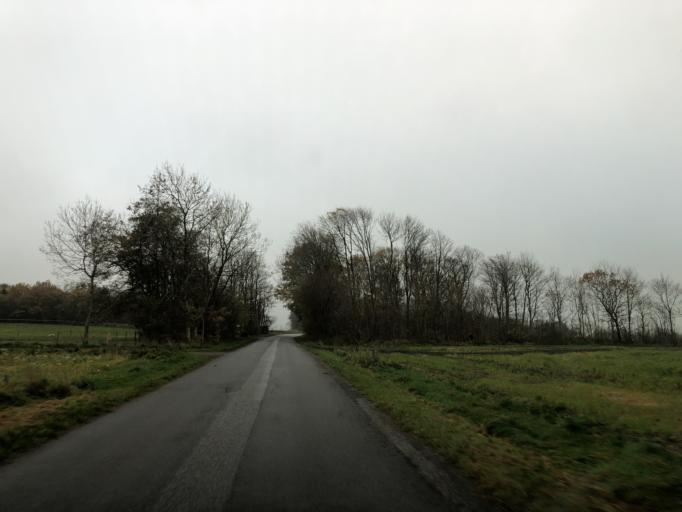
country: DK
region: Central Jutland
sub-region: Herning Kommune
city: Vildbjerg
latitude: 56.2233
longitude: 8.7726
